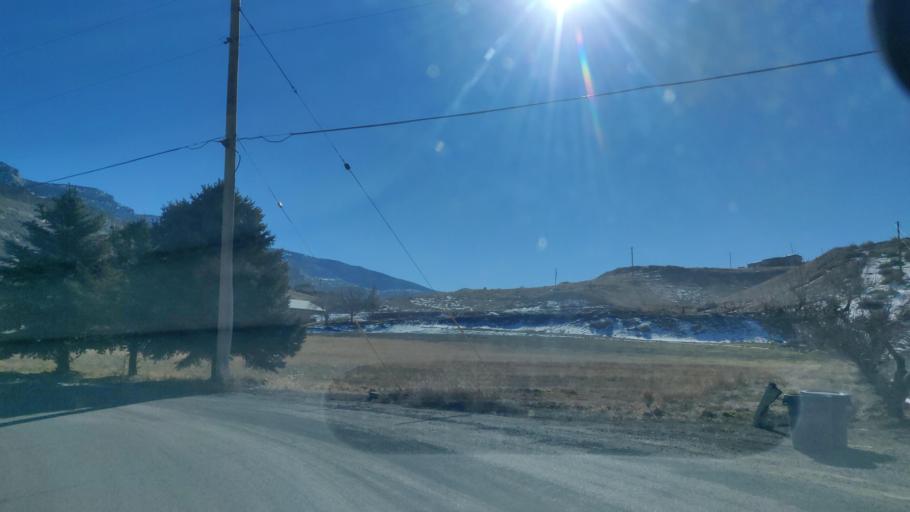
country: US
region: Colorado
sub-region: Mesa County
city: Palisade
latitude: 39.1023
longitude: -108.3343
